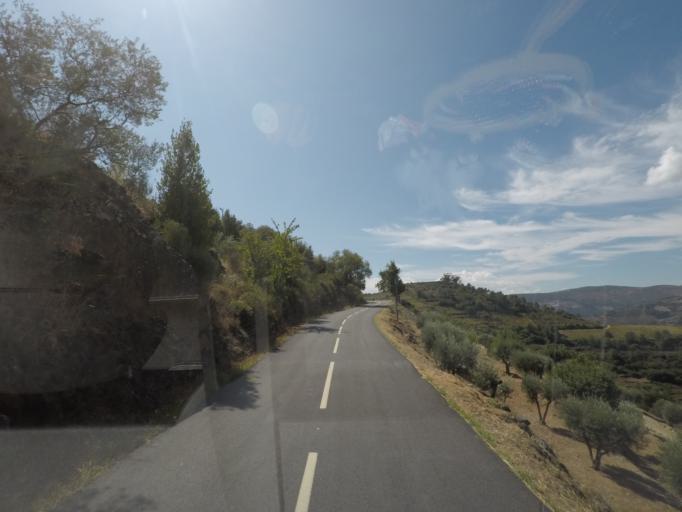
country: PT
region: Vila Real
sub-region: Sabrosa
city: Sabrosa
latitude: 41.2176
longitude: -7.5262
